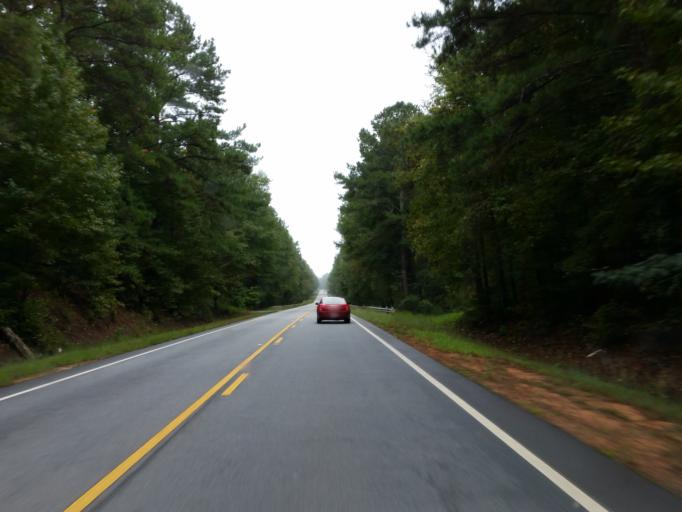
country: US
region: Georgia
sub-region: Crawford County
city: Roberta
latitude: 32.8603
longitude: -84.0822
